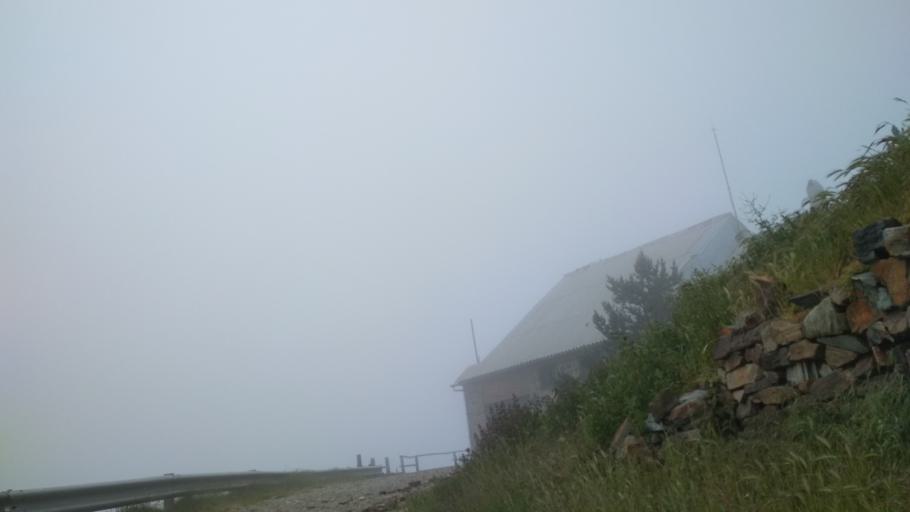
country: ES
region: Catalonia
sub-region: Provincia de Barcelona
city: Fogars de Montclus
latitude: 41.7765
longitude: 2.4352
